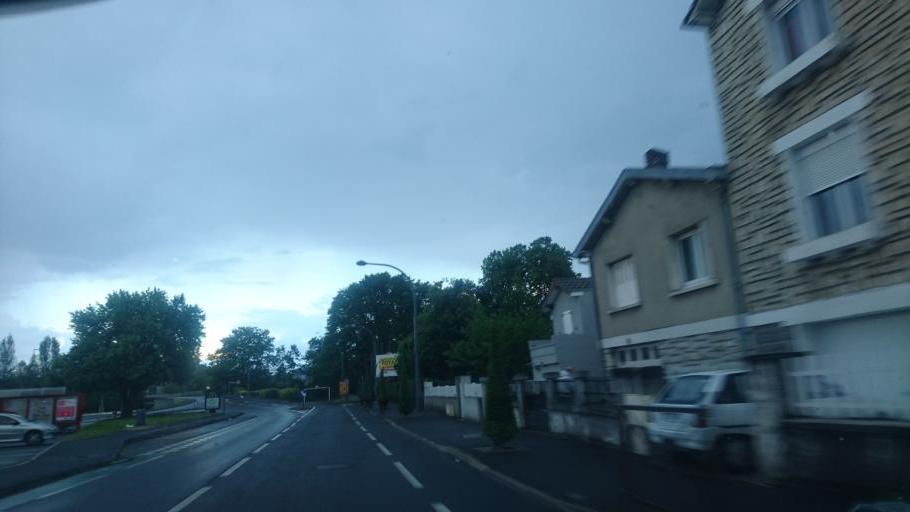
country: FR
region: Limousin
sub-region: Departement de la Correze
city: Malemort-sur-Correze
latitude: 45.1674
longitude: 1.5607
